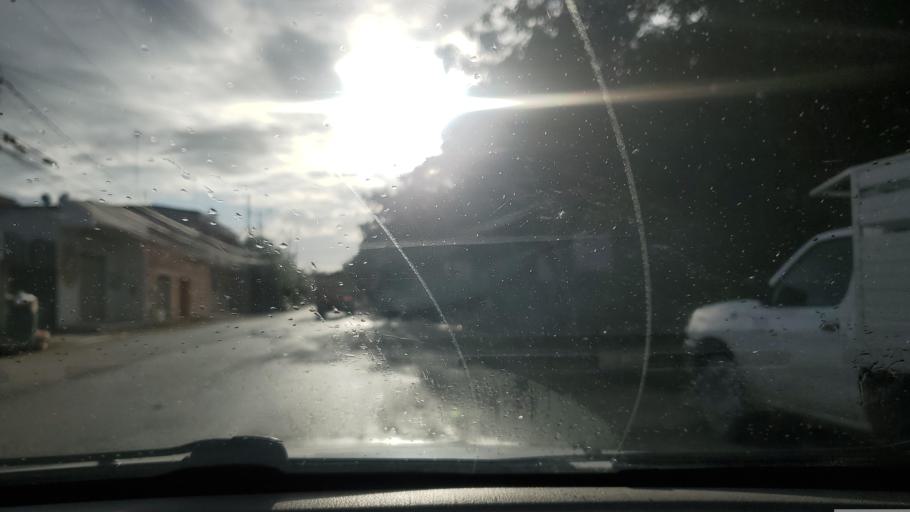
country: MX
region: Quintana Roo
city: Tulum
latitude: 20.2102
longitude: -87.4722
